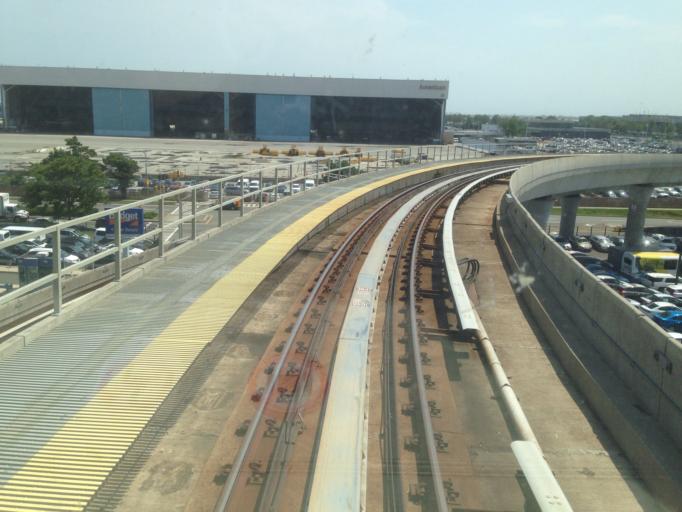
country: US
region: New York
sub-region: Queens County
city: Jamaica
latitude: 40.6592
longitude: -73.8036
